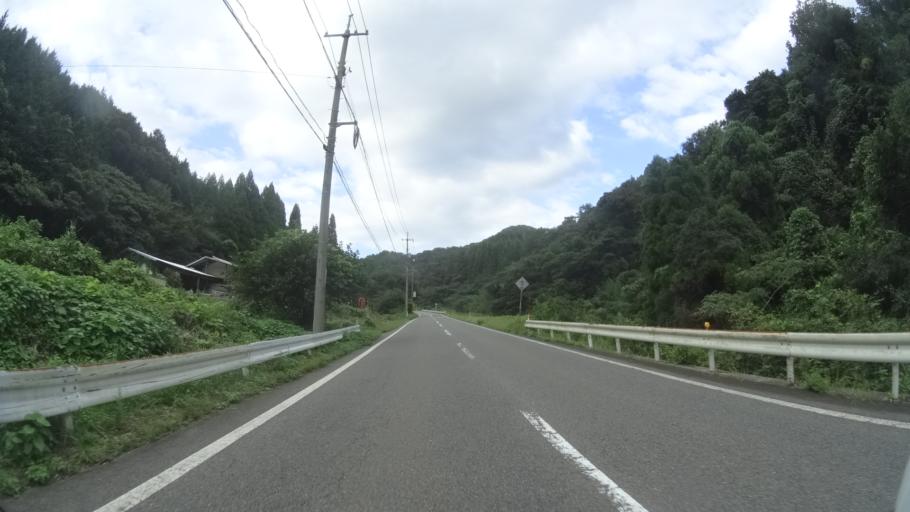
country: JP
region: Tottori
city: Kurayoshi
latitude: 35.4220
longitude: 133.9216
